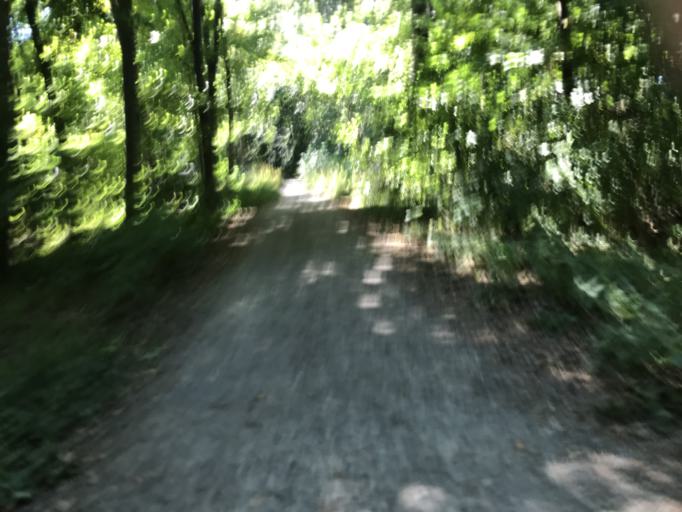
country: DE
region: Baden-Wuerttemberg
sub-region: Regierungsbezirk Stuttgart
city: Stuttgart
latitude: 48.7528
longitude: 9.1782
